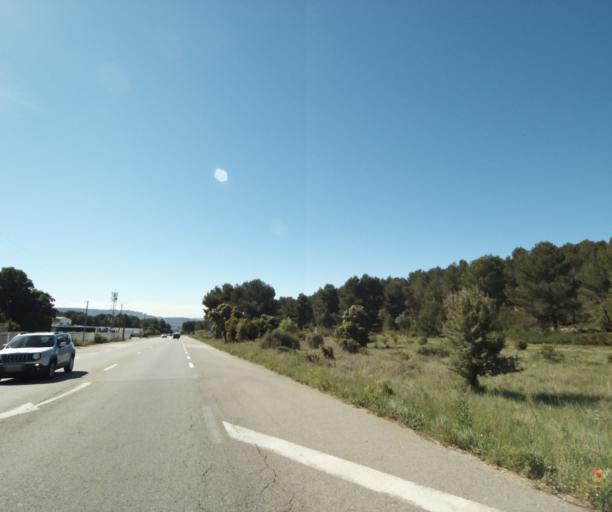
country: FR
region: Provence-Alpes-Cote d'Azur
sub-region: Departement des Bouches-du-Rhone
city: Rognac
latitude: 43.5090
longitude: 5.2061
